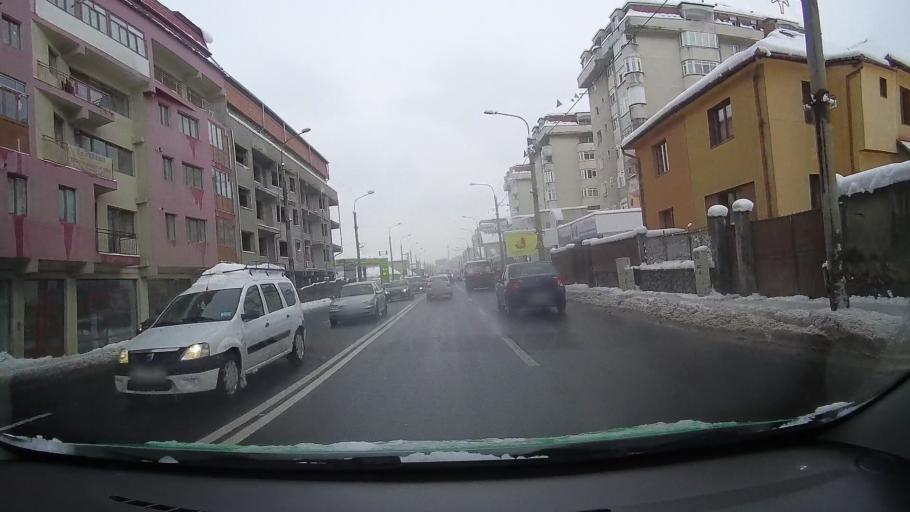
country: RO
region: Sibiu
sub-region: Municipiul Sibiu
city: Sibiu
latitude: 45.7935
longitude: 24.1239
